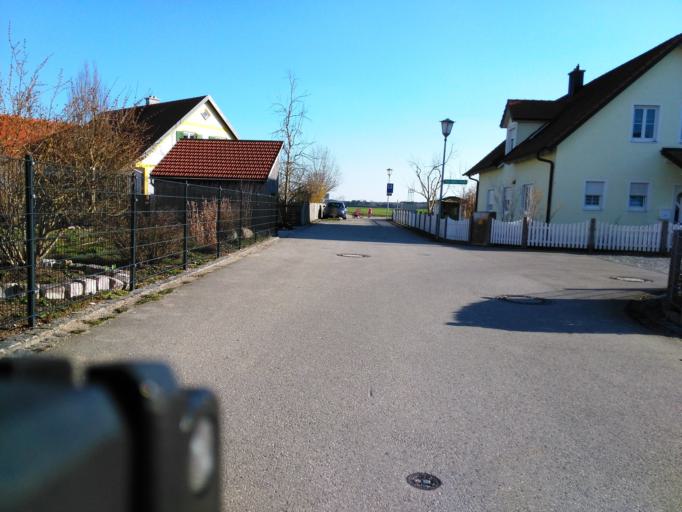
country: DE
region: Bavaria
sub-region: Upper Bavaria
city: Mammendorf
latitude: 48.2038
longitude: 11.1574
